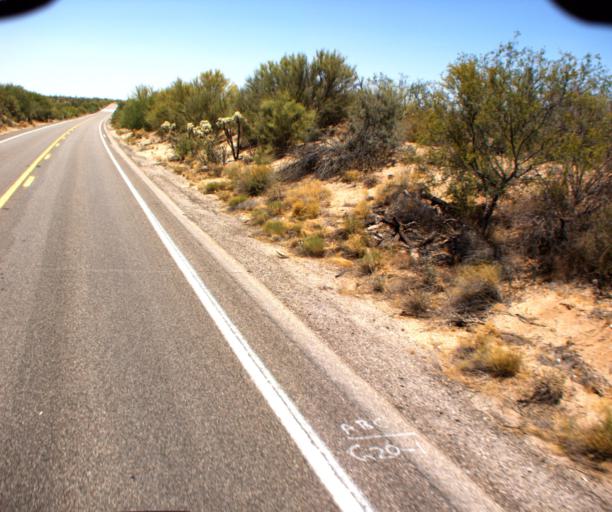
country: US
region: Arizona
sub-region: Pima County
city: Marana
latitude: 32.7705
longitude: -111.1583
